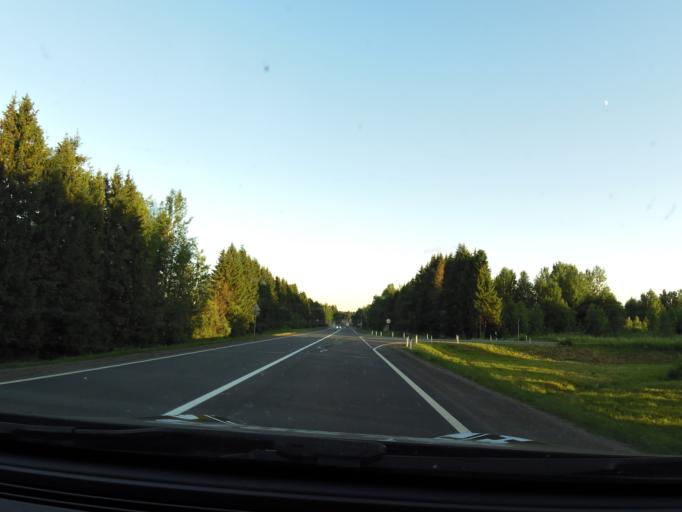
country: RU
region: Jaroslavl
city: Prechistoye
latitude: 58.4697
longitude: 40.3213
